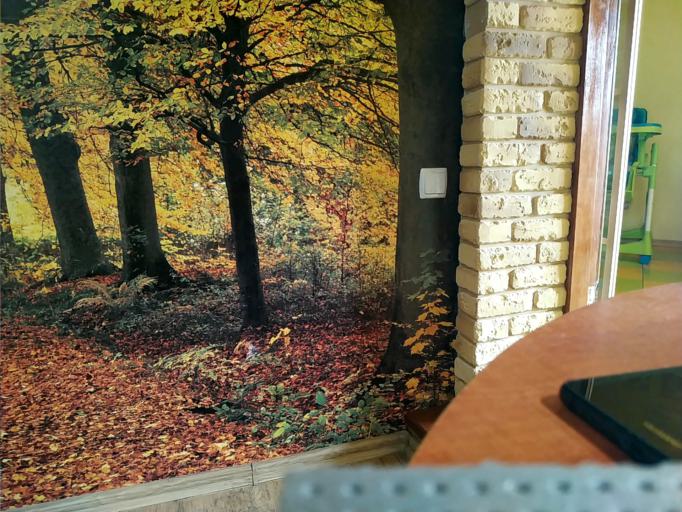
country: RU
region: Tverskaya
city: Kalashnikovo
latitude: 57.2960
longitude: 35.0981
